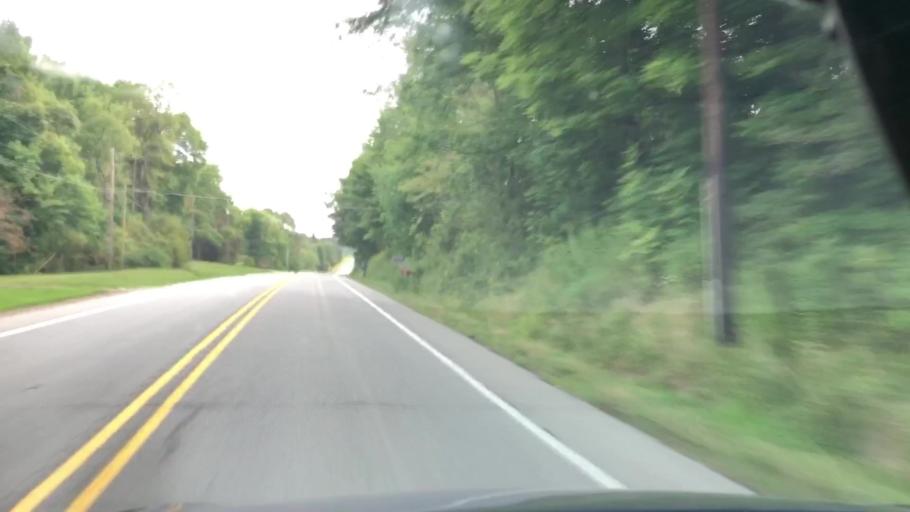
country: US
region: Pennsylvania
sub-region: Crawford County
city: Titusville
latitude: 41.6020
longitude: -79.6775
